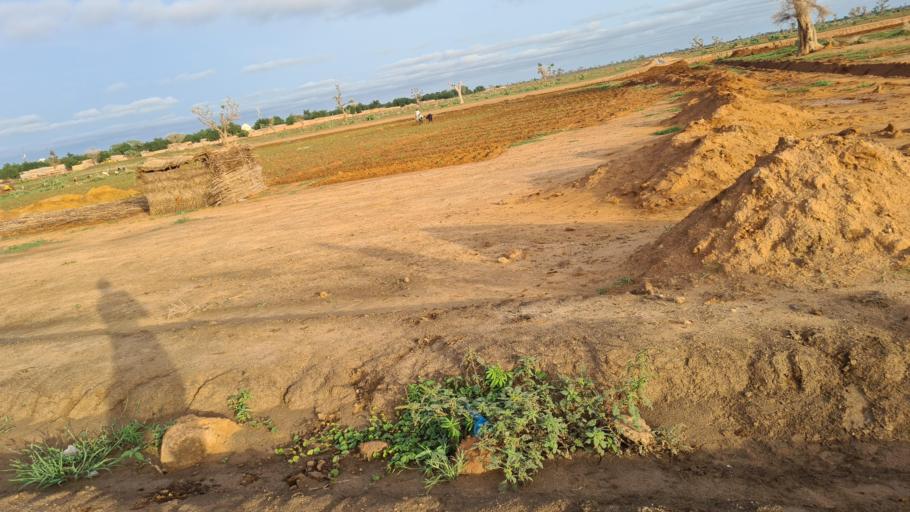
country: NE
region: Tahoua
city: Birni N Konni
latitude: 13.7890
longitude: 5.2356
